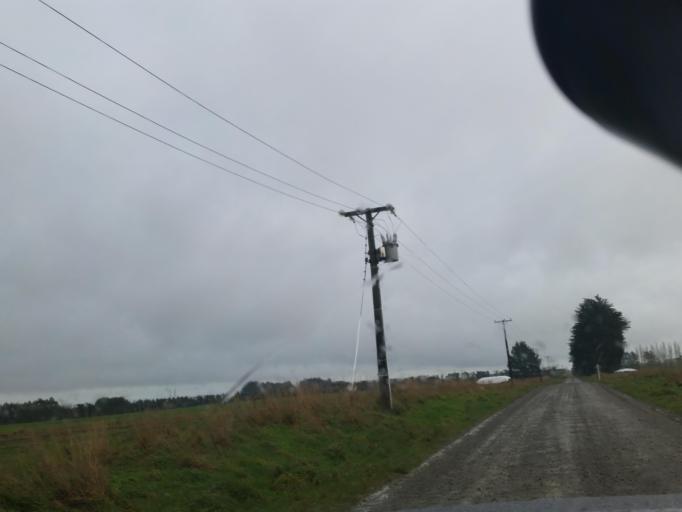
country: NZ
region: Southland
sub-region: Southland District
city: Winton
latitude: -46.2269
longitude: 168.2795
